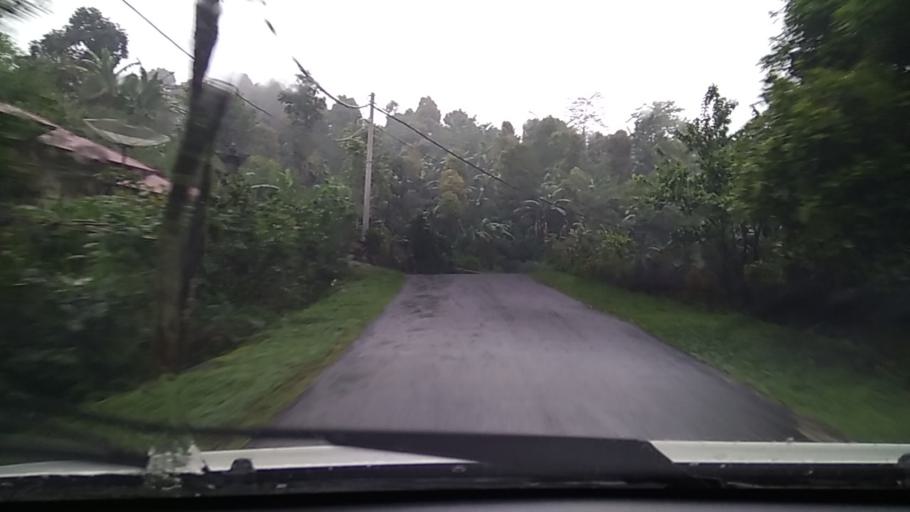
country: ID
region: Bali
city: Banjar Ambengan
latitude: -8.2122
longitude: 115.1715
